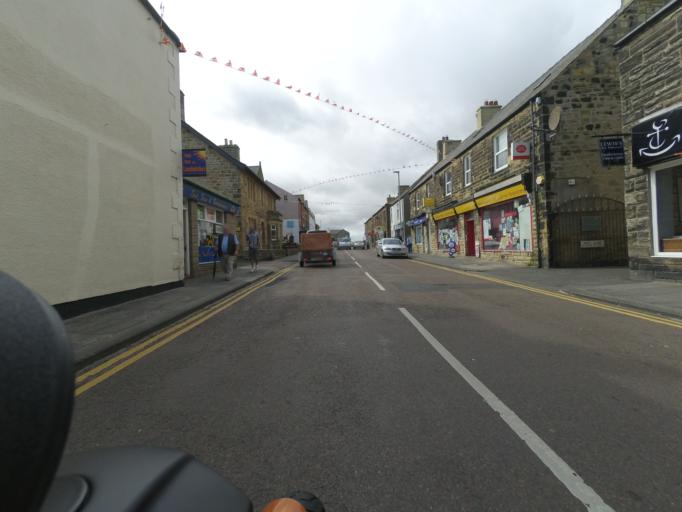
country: GB
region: England
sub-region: Northumberland
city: North Sunderland
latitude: 55.5813
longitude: -1.6539
